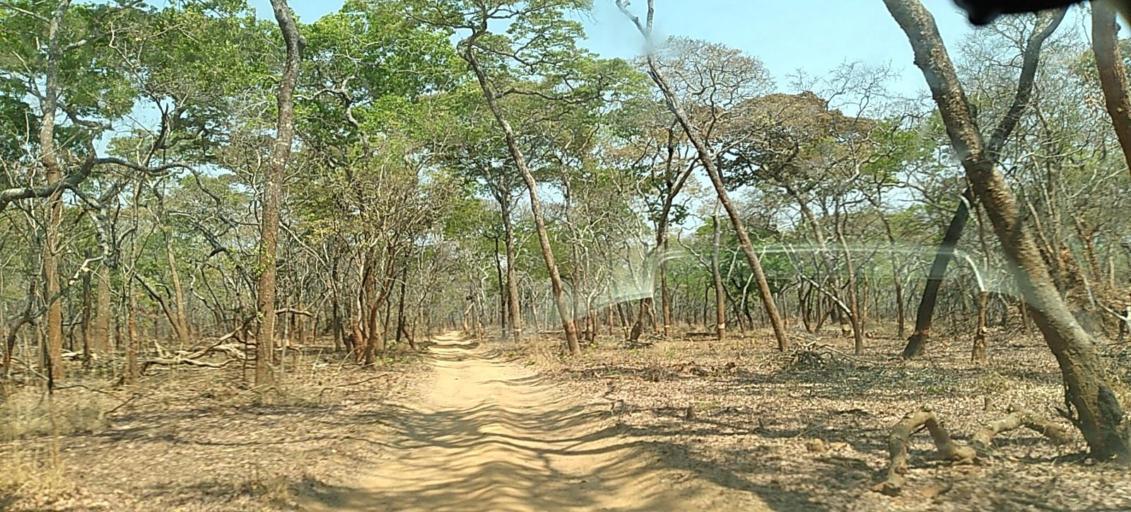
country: ZM
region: North-Western
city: Kasempa
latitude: -13.3928
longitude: 25.6087
